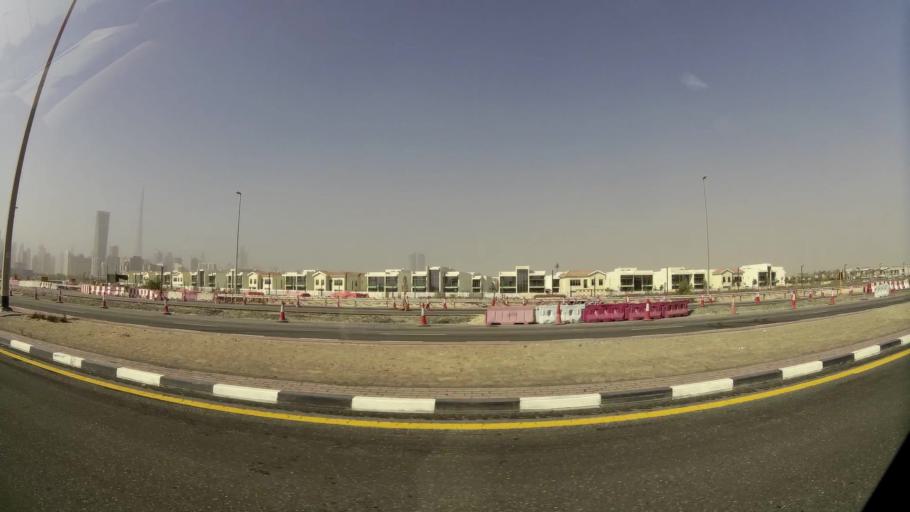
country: AE
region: Dubai
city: Dubai
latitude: 25.1642
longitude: 55.2713
